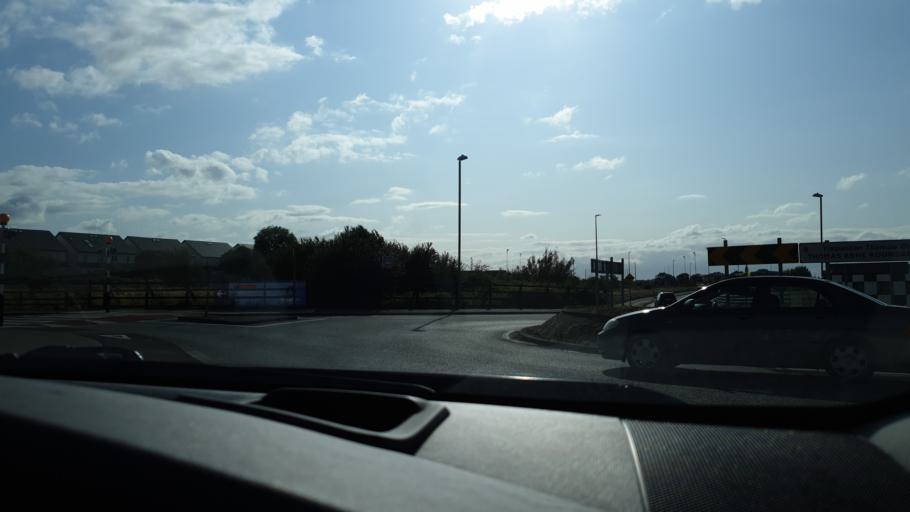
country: IE
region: Leinster
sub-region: An Mhi
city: Ashbourne
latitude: 53.5101
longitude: -6.4041
